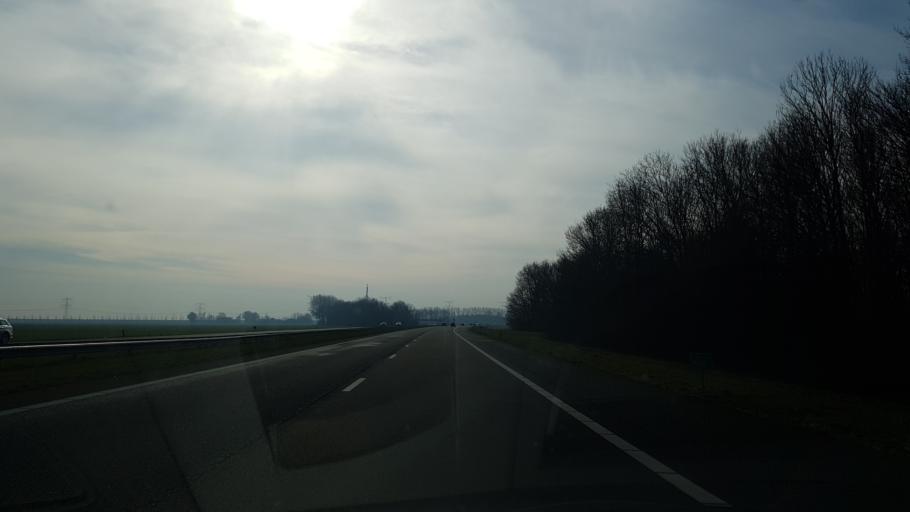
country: NL
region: Flevoland
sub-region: Gemeente Urk
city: Urk
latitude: 52.6320
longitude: 5.6695
